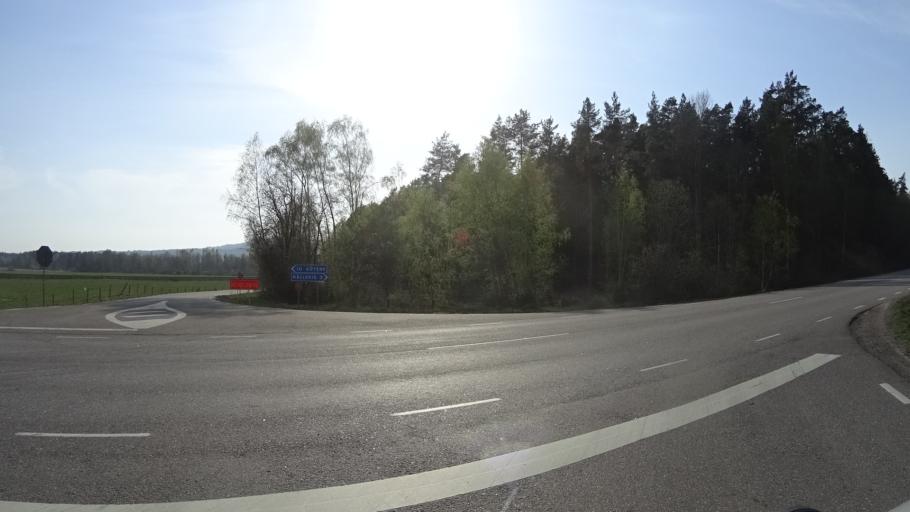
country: SE
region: Vaestra Goetaland
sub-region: Gotene Kommun
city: Goetene
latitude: 58.6196
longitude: 13.4829
